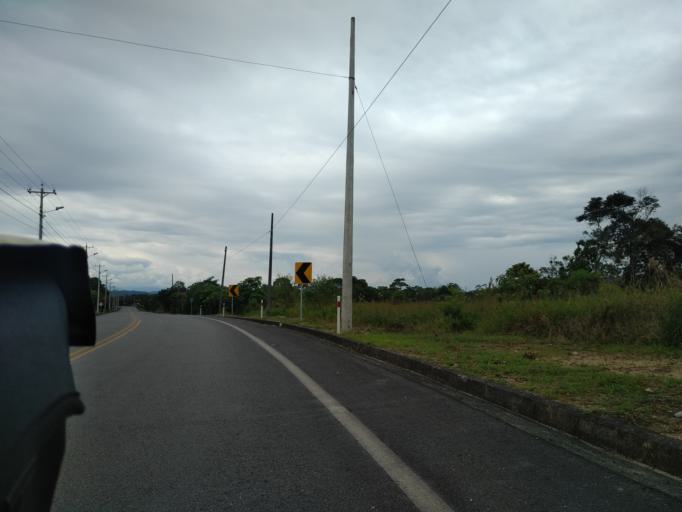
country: EC
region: Napo
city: Tena
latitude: -1.2044
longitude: -77.8738
